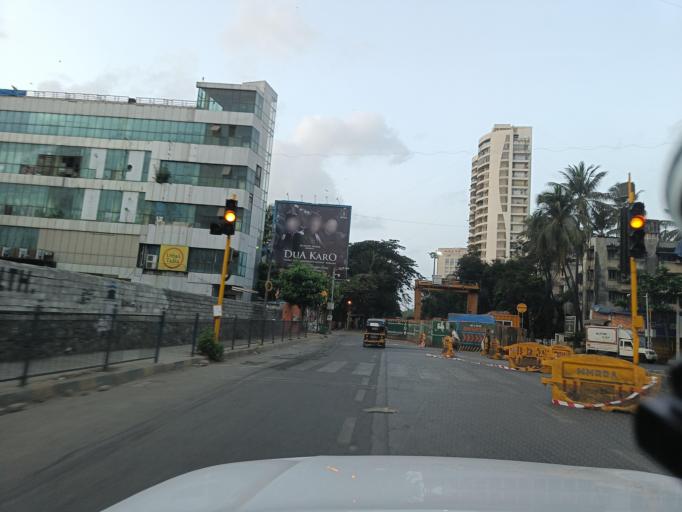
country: IN
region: Maharashtra
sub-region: Mumbai Suburban
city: Powai
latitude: 19.1349
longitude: 72.8257
